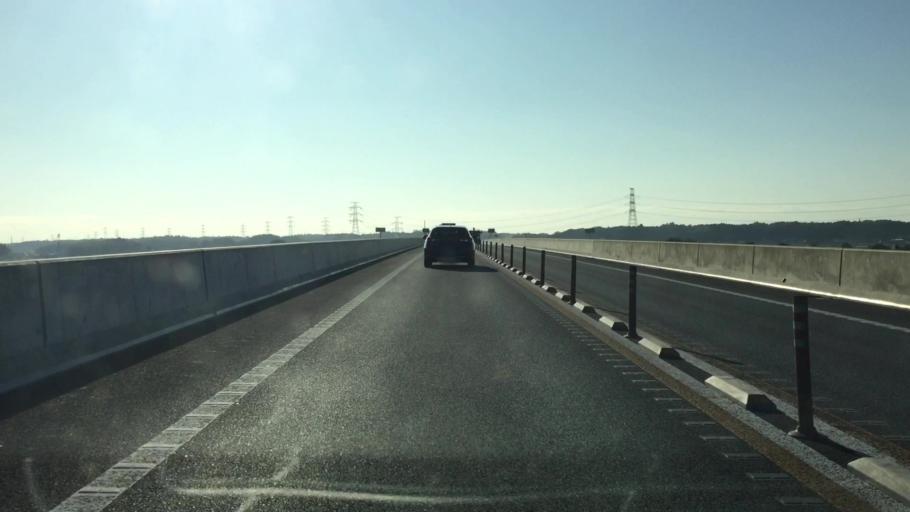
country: JP
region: Ibaraki
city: Inashiki
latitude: 35.9038
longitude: 140.3749
